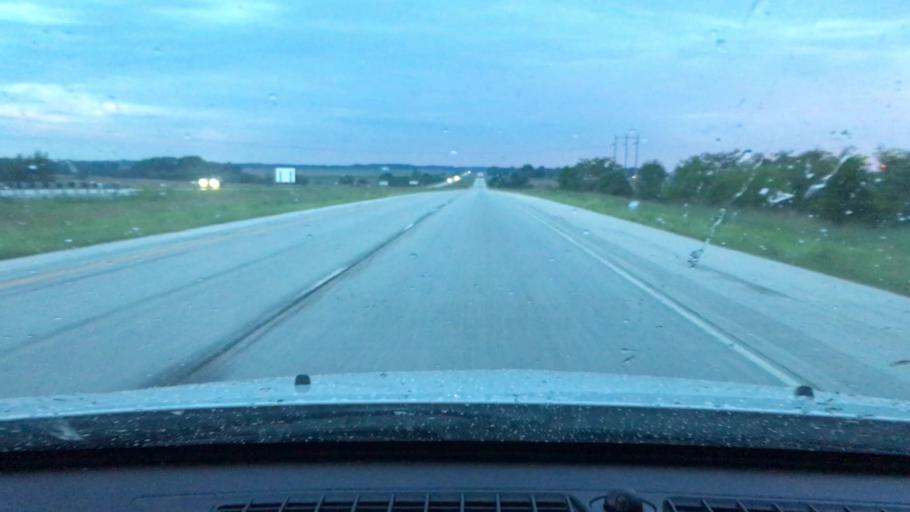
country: US
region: Illinois
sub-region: Morgan County
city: South Jacksonville
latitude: 39.7097
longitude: -90.1816
